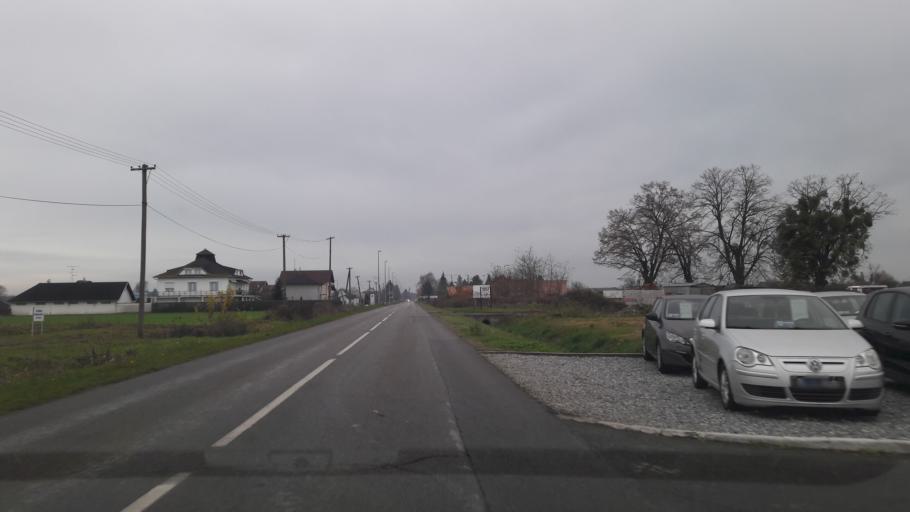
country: HR
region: Osjecko-Baranjska
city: Josipovac
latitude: 45.5915
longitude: 18.5708
